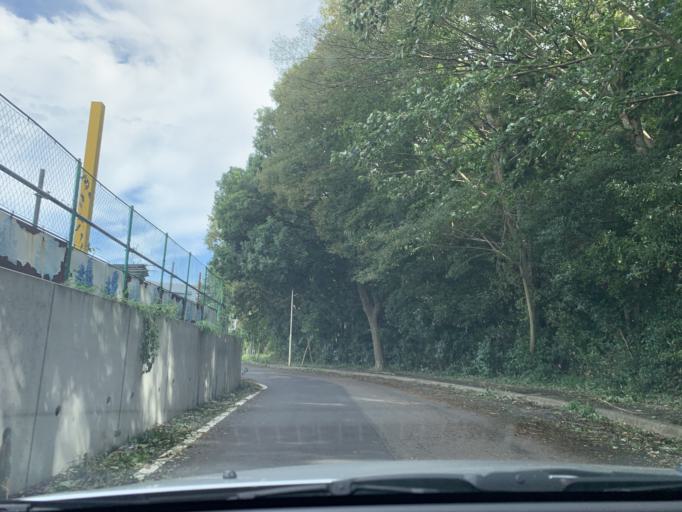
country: JP
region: Chiba
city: Nagareyama
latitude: 35.8978
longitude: 139.8978
